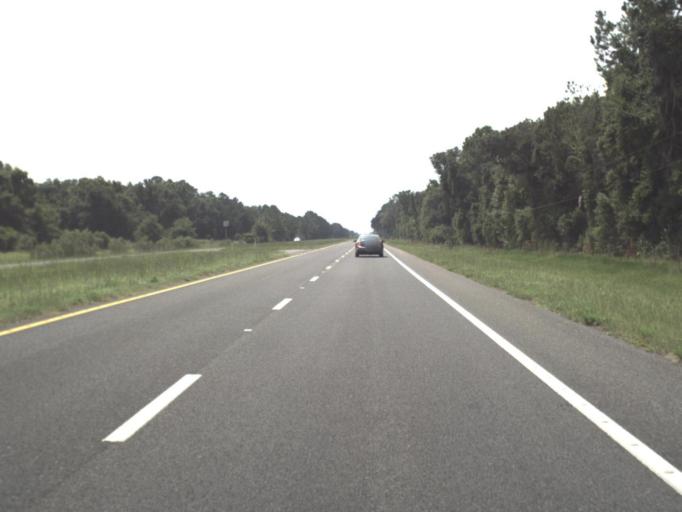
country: US
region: Florida
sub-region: Levy County
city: Chiefland
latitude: 29.4533
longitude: -82.8458
